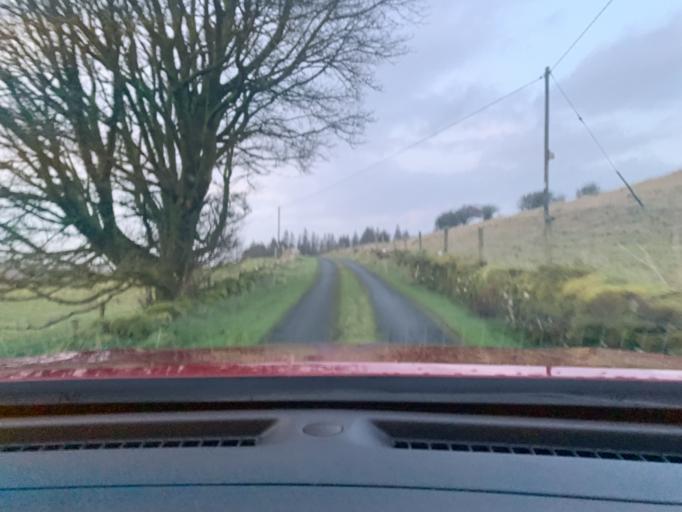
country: IE
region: Connaught
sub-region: Sligo
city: Ballymote
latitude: 54.0554
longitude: -8.3962
